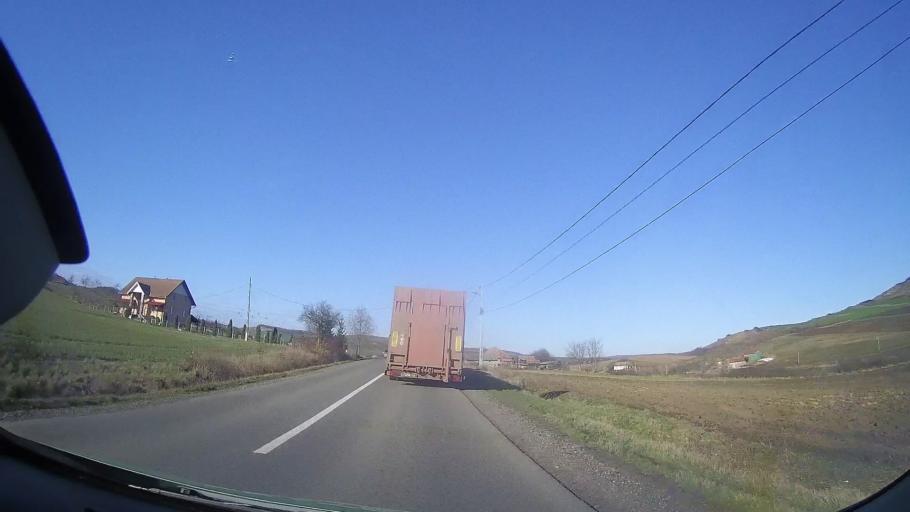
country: RO
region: Mures
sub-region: Comuna Sarmasu
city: Balda
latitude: 46.7164
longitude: 24.1486
